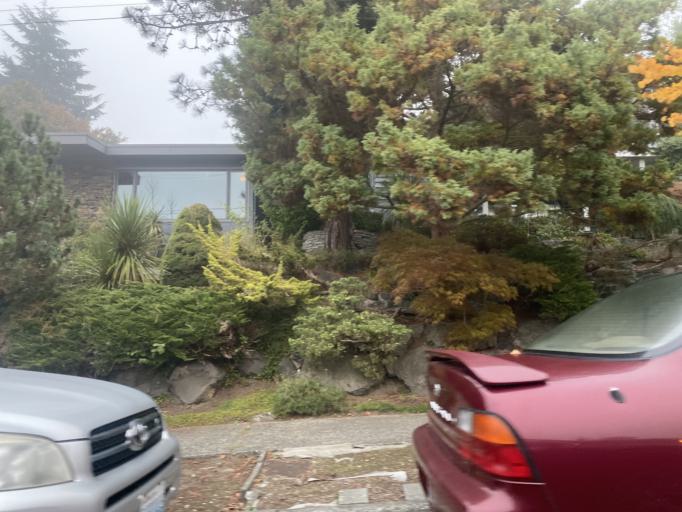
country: US
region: Washington
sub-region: King County
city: Seattle
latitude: 47.6515
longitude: -122.4069
